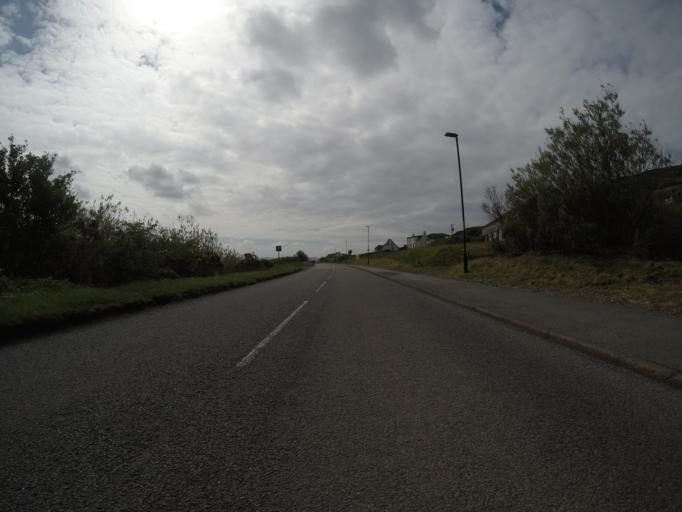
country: GB
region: Scotland
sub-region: Highland
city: Portree
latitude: 57.5900
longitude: -6.3722
